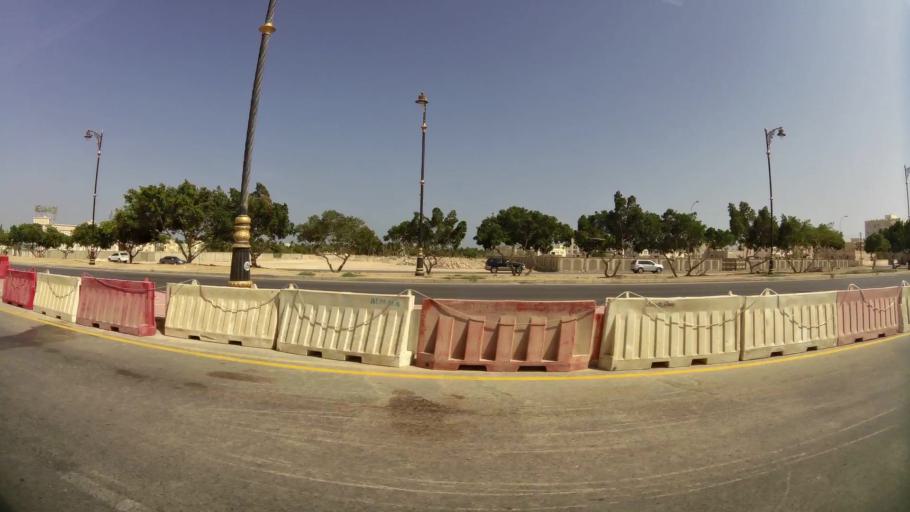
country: OM
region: Zufar
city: Salalah
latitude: 17.0230
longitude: 54.0706
